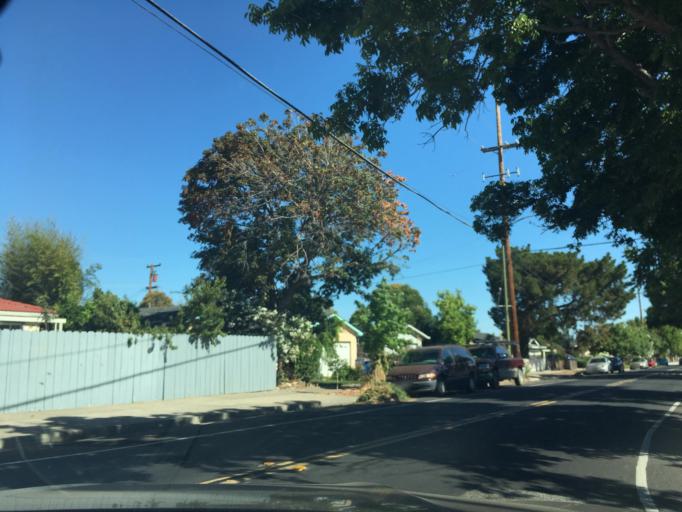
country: US
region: California
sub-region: Santa Clara County
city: Cambrian Park
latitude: 37.2364
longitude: -121.9129
